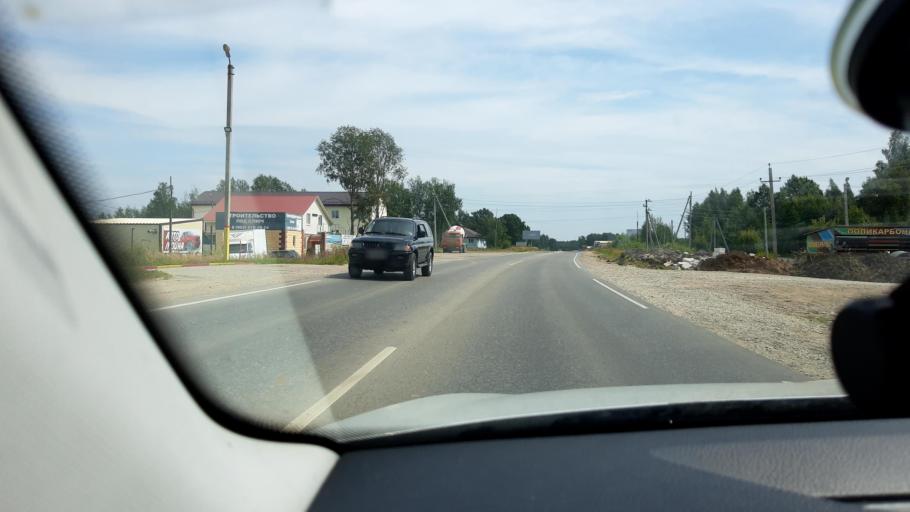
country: RU
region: Tula
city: Zaokskiy
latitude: 54.7477
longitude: 37.4040
